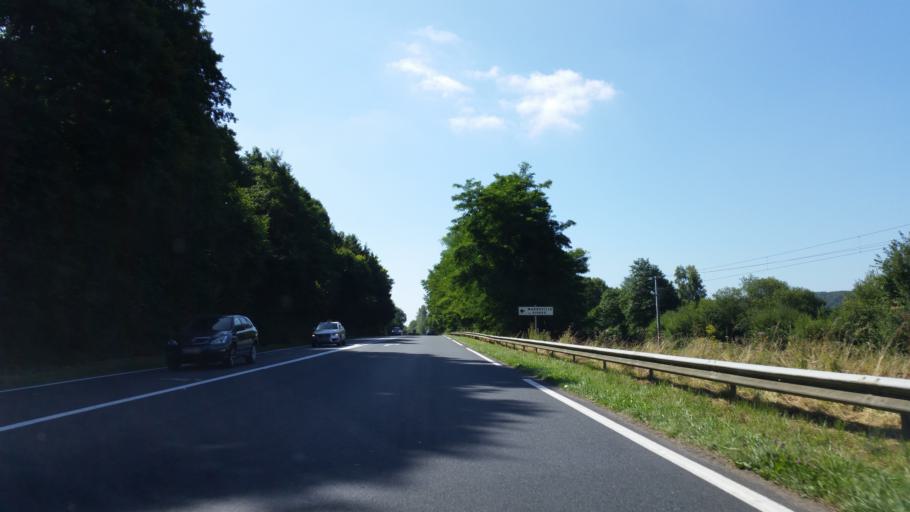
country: FR
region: Lower Normandy
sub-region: Departement du Calvados
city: Saint-Gatien-des-Bois
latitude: 49.2657
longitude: 0.2172
